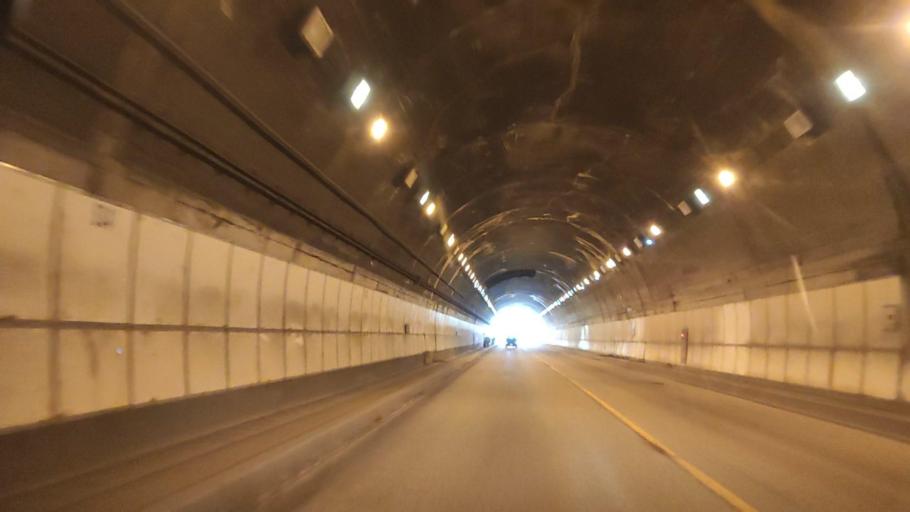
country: JP
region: Aomori
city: Aomori Shi
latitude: 40.8574
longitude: 140.8413
